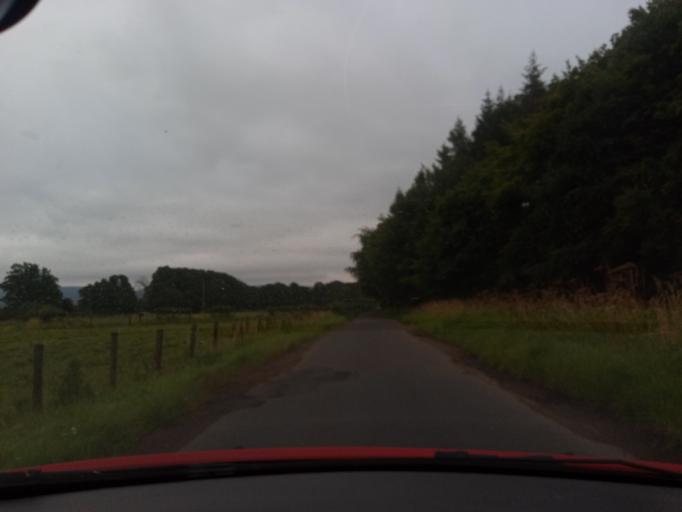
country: GB
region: England
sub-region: Northumberland
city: Otterburn
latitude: 55.3223
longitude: -2.0707
